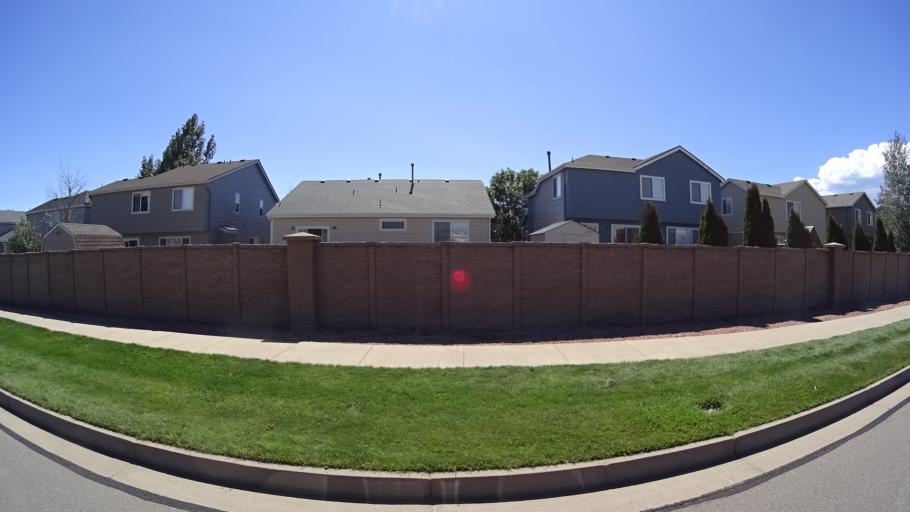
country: US
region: Colorado
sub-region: El Paso County
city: Security-Widefield
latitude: 38.7855
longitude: -104.7301
